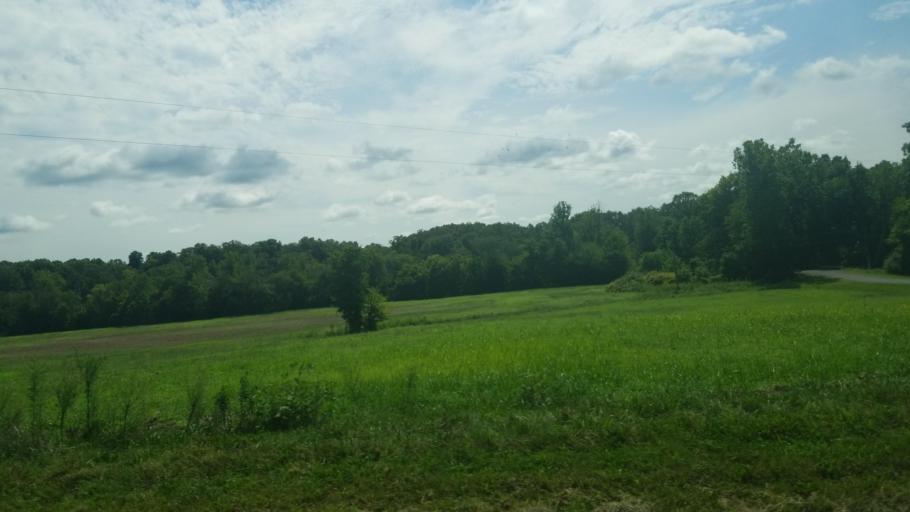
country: US
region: Illinois
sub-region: Saline County
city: Carrier Mills
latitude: 37.7984
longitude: -88.7437
